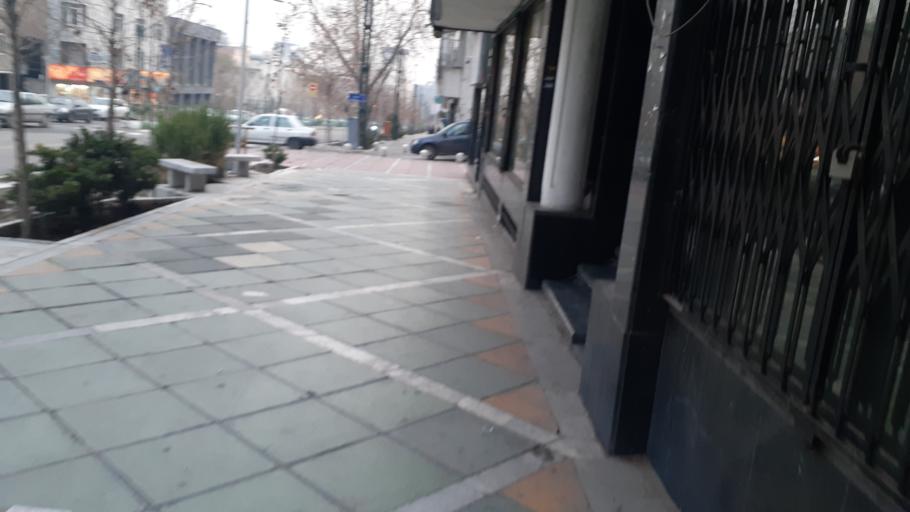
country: IR
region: Tehran
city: Tehran
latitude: 35.7447
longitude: 51.4108
